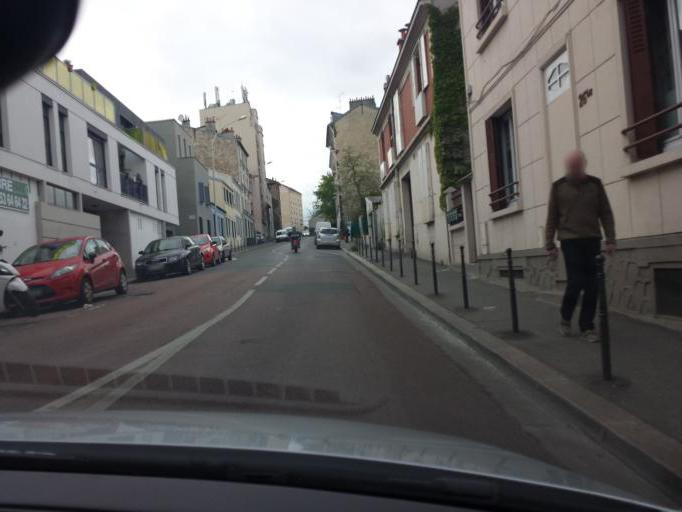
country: FR
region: Ile-de-France
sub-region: Departement du Val-de-Marne
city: Ivry-sur-Seine
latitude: 48.8168
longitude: 2.3780
